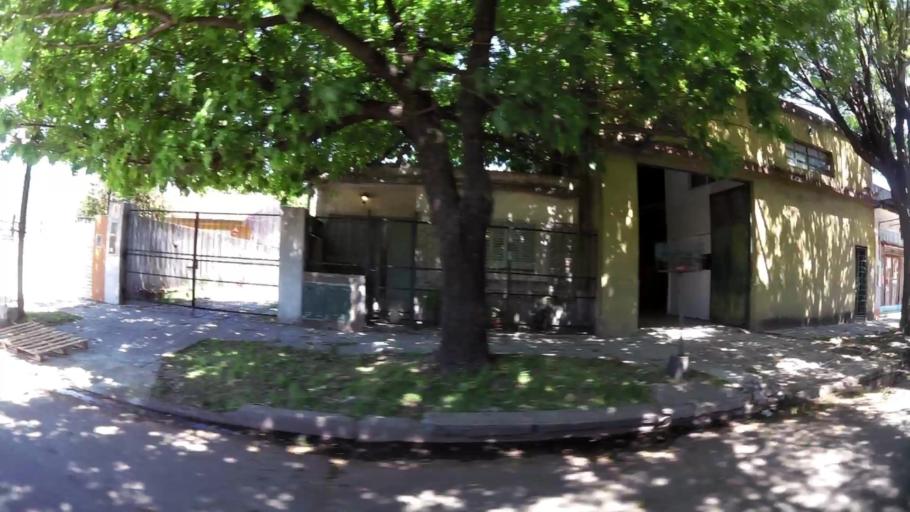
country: AR
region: Buenos Aires
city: Caseros
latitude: -34.5689
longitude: -58.5700
